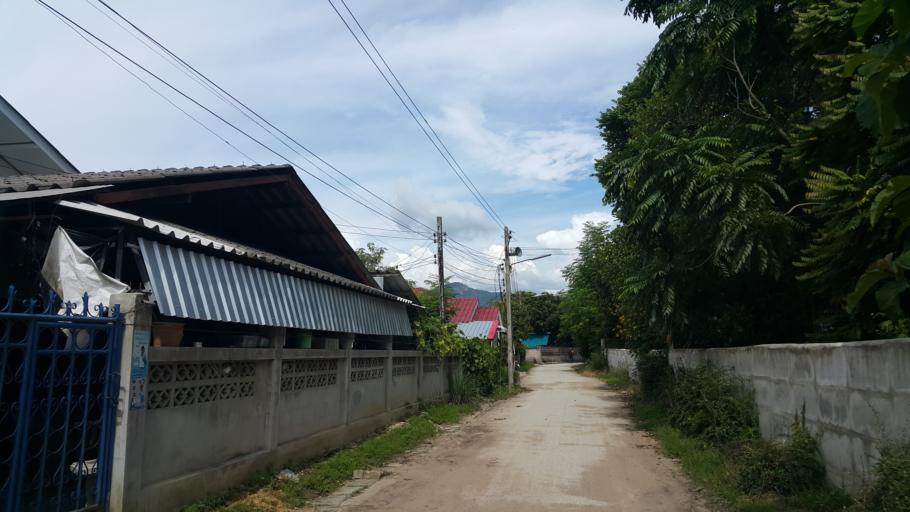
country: TH
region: Chiang Mai
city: San Kamphaeng
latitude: 18.7251
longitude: 99.1906
